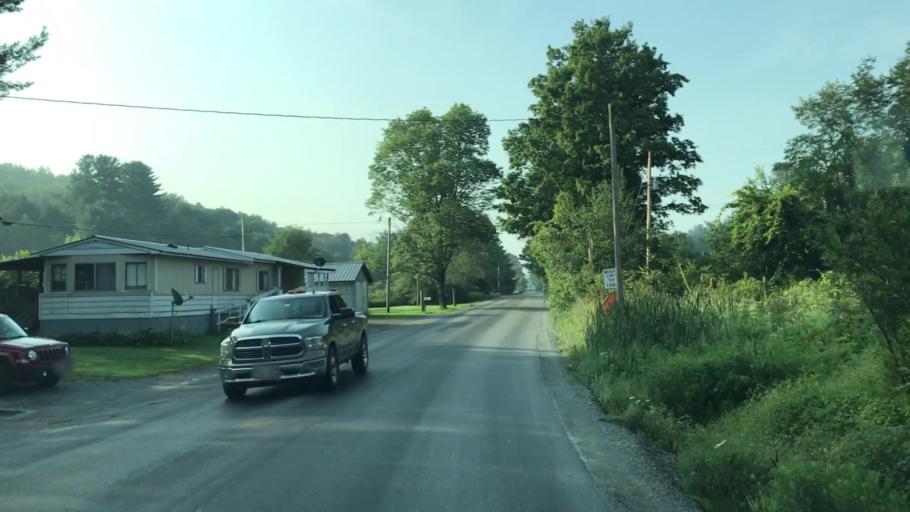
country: US
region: Pennsylvania
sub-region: Wyoming County
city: Factoryville
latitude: 41.6564
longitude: -75.7996
